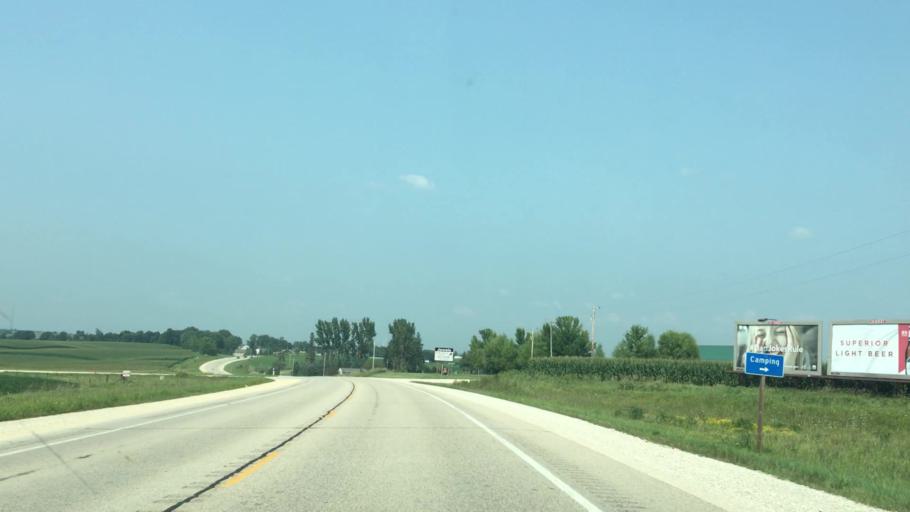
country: US
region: Iowa
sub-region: Winneshiek County
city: Decorah
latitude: 43.2542
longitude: -91.8388
